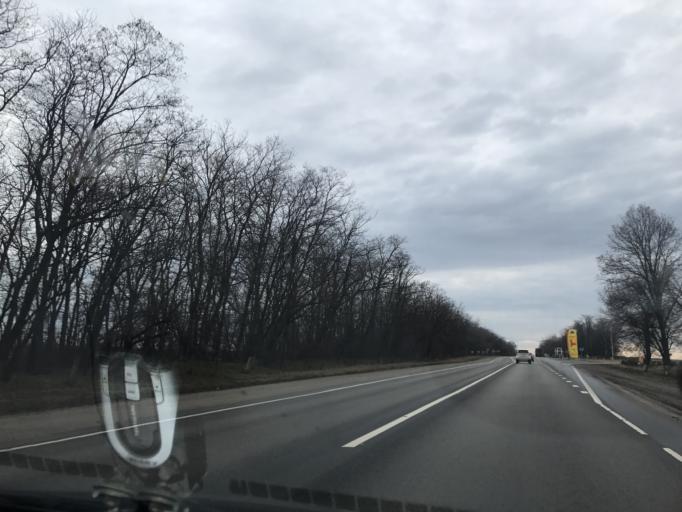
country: RU
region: Krasnodarskiy
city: Alekseyevskaya
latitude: 45.6925
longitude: 40.3040
